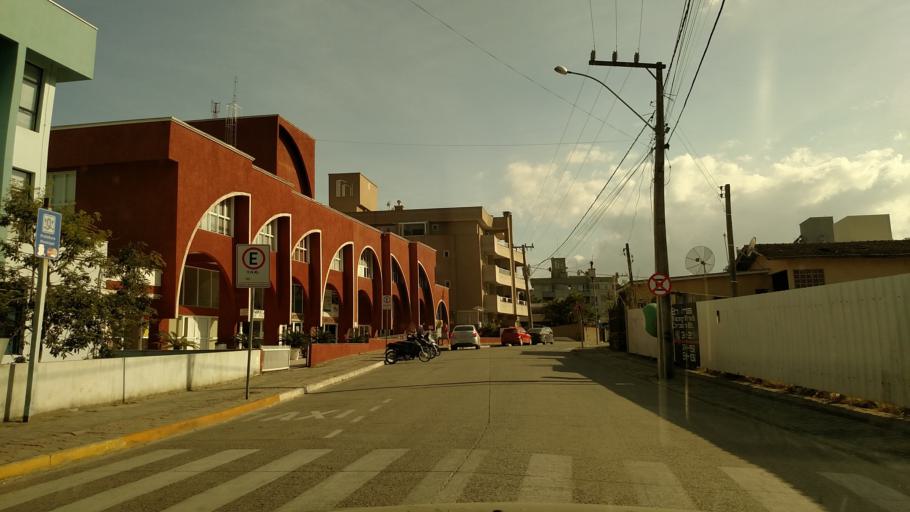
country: BR
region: Santa Catarina
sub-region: Porto Belo
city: Porto Belo
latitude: -27.1523
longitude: -48.5011
